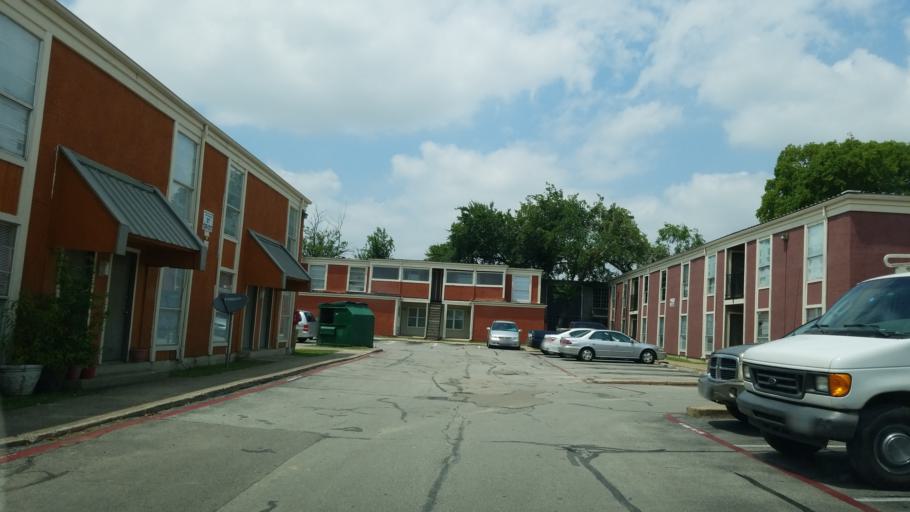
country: US
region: Texas
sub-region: Dallas County
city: Farmers Branch
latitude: 32.9059
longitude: -96.8812
